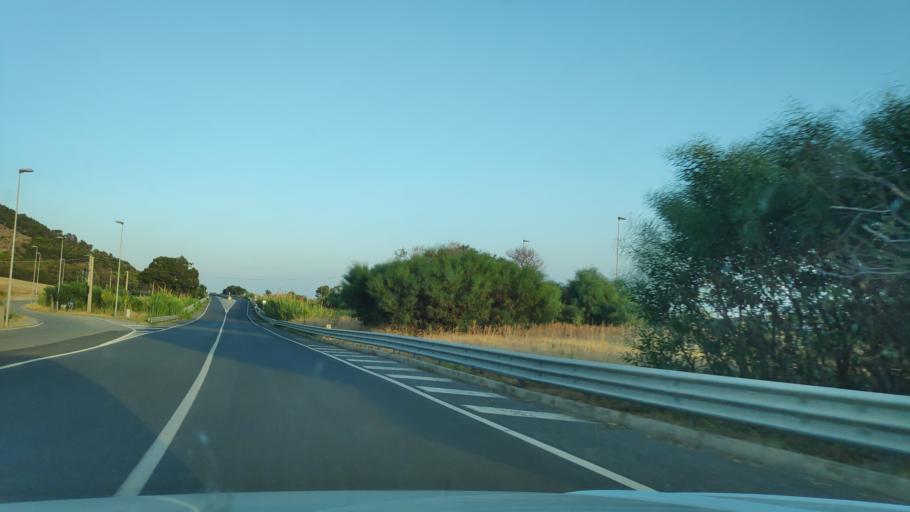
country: IT
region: Calabria
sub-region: Provincia di Reggio Calabria
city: Palizzi Marina
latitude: 37.9227
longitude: 15.9552
